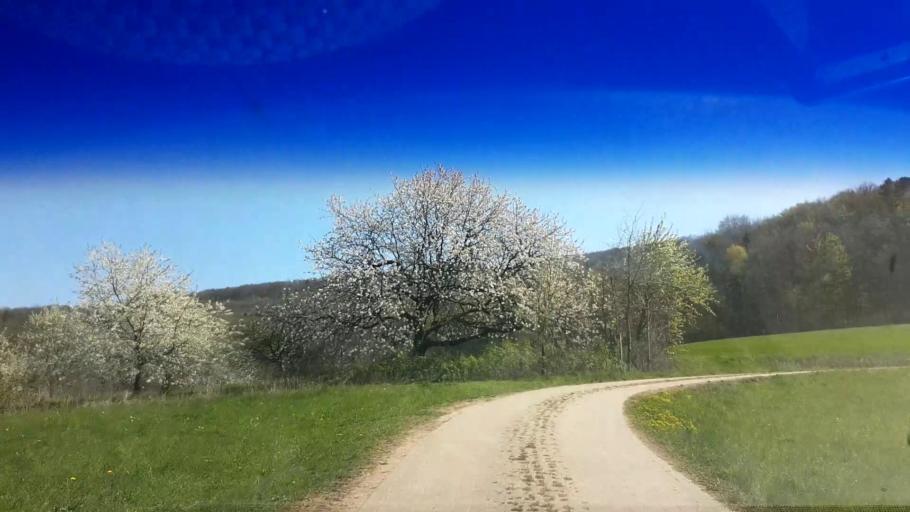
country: DE
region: Bavaria
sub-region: Upper Franconia
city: Schesslitz
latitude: 49.9434
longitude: 11.0458
